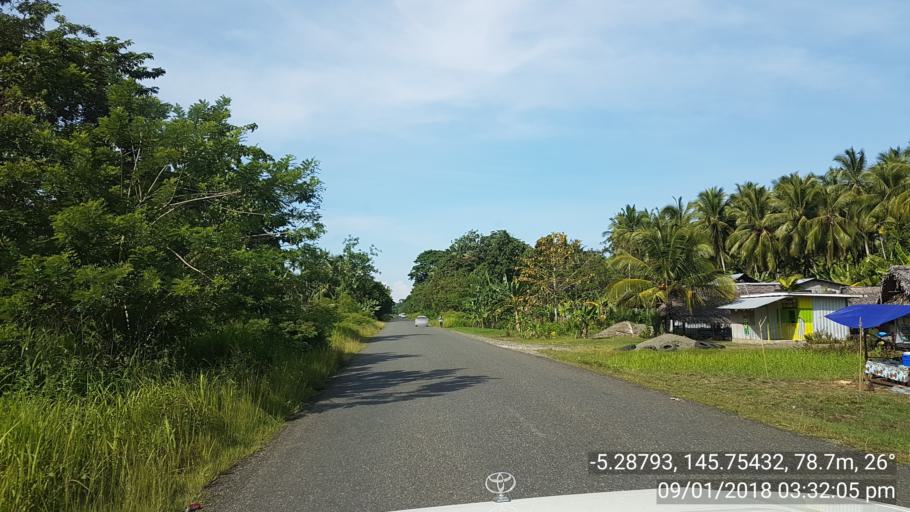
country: PG
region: Madang
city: Madang
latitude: -5.2881
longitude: 145.7544
